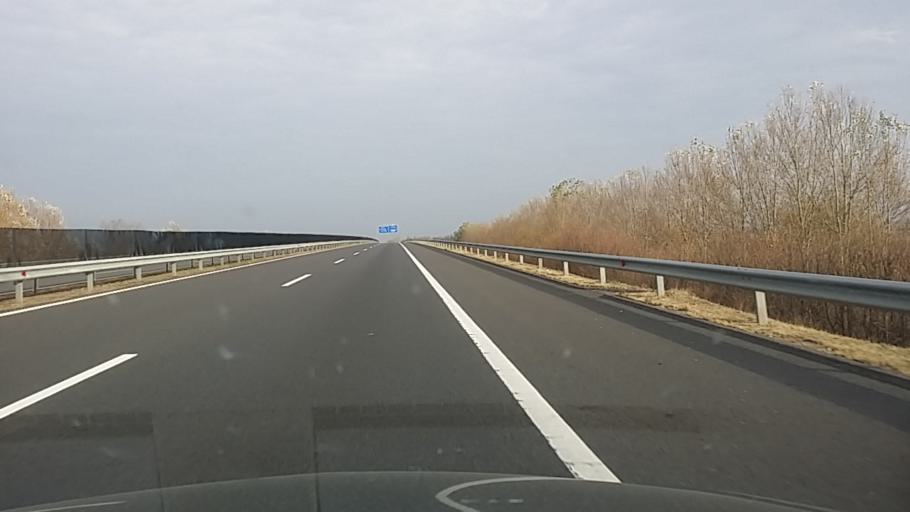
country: HU
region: Szabolcs-Szatmar-Bereg
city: Nagykallo
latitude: 47.8890
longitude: 21.7717
